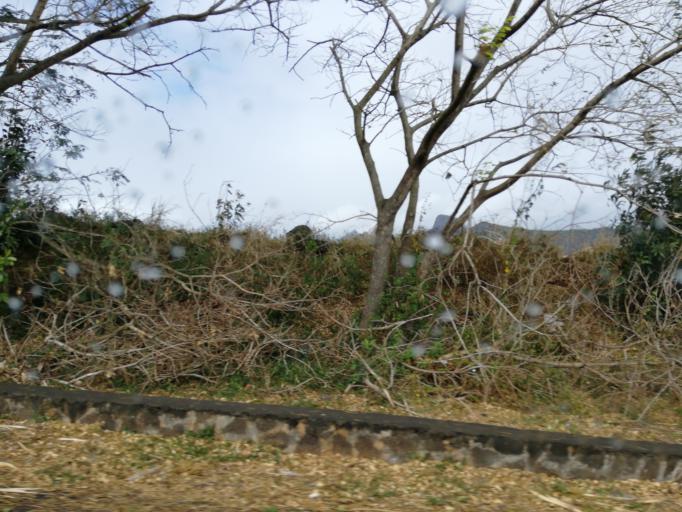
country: MU
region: Pamplemousses
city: Long Mountain
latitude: -20.1251
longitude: 57.5694
